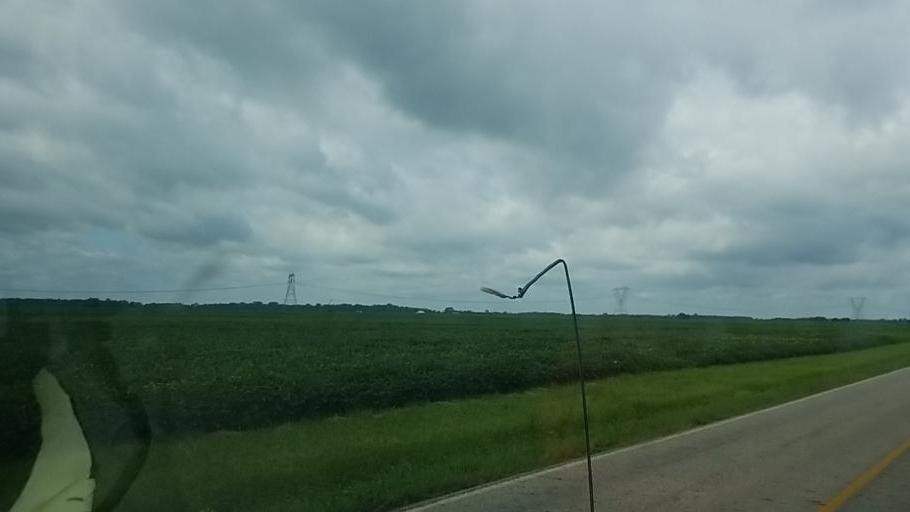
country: US
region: Ohio
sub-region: Madison County
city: Mount Sterling
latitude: 39.7748
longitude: -83.2138
